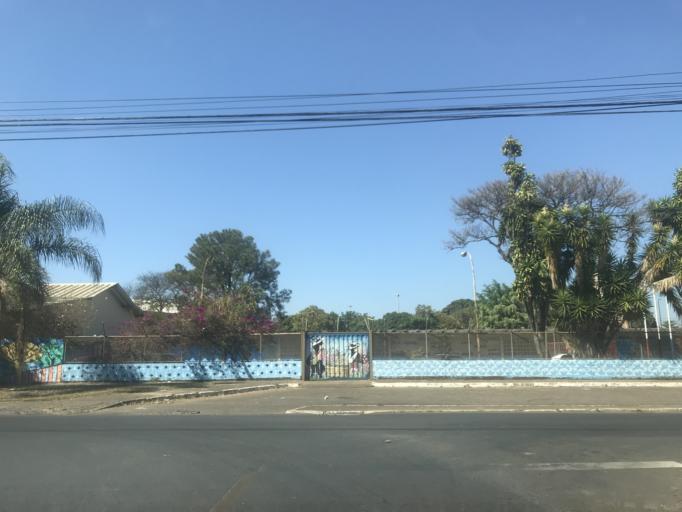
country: BR
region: Federal District
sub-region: Brasilia
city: Brasilia
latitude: -15.8181
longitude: -47.9877
